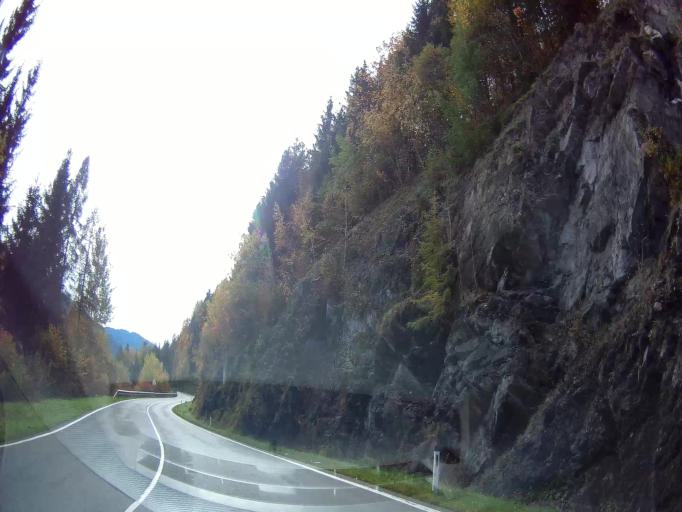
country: AT
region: Salzburg
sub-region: Politischer Bezirk Sankt Johann im Pongau
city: Bischofshofen
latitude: 47.4076
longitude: 13.2122
